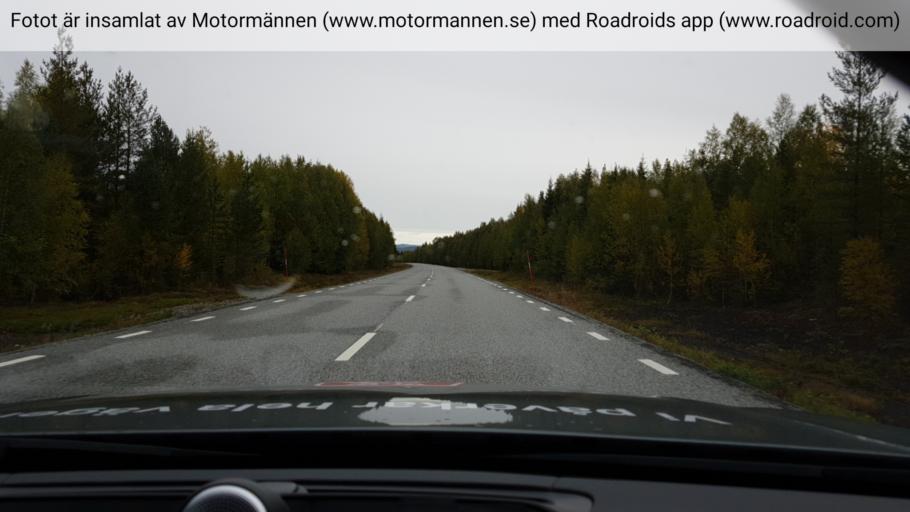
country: SE
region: Jaemtland
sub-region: Stroemsunds Kommun
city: Stroemsund
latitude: 64.1321
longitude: 15.6630
